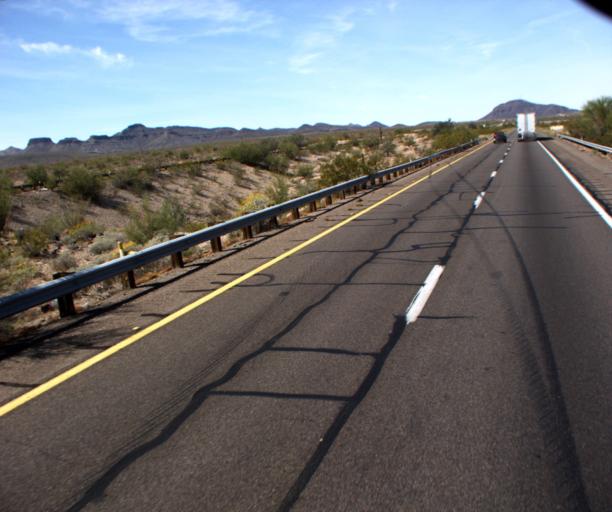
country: US
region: Arizona
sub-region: La Paz County
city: Quartzsite
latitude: 33.6583
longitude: -113.9801
